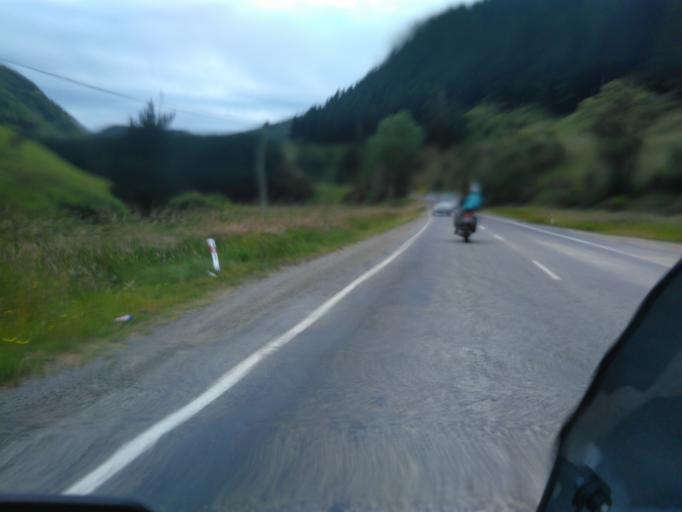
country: NZ
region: Bay of Plenty
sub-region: Opotiki District
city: Opotiki
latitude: -38.3802
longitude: 177.4755
